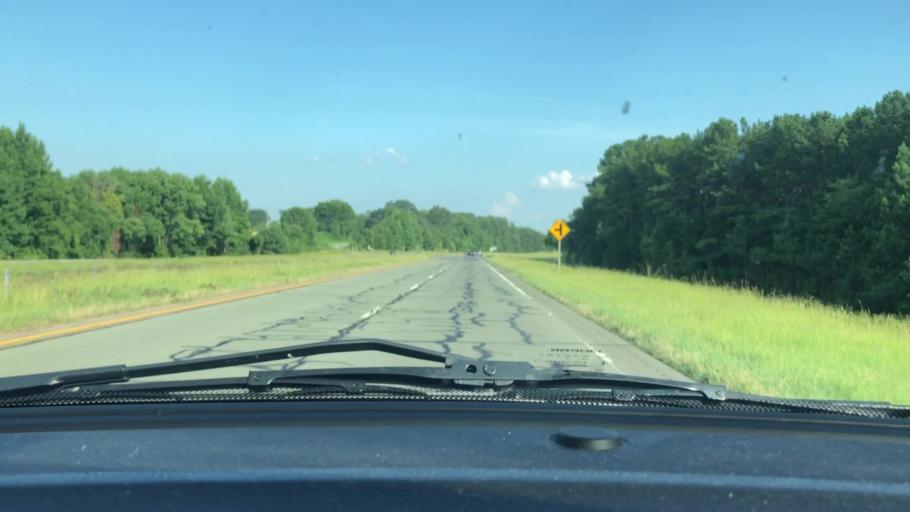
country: US
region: North Carolina
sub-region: Chatham County
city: Siler City
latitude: 35.6858
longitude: -79.4209
